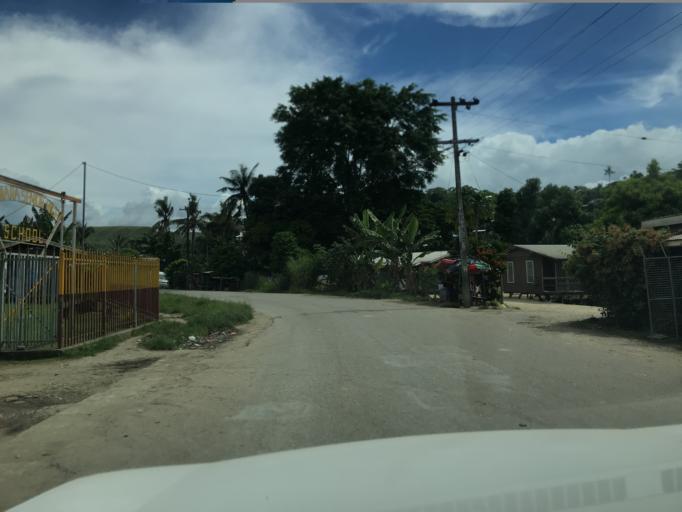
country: SB
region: Guadalcanal
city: Honiara
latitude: -9.4399
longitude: 159.9620
